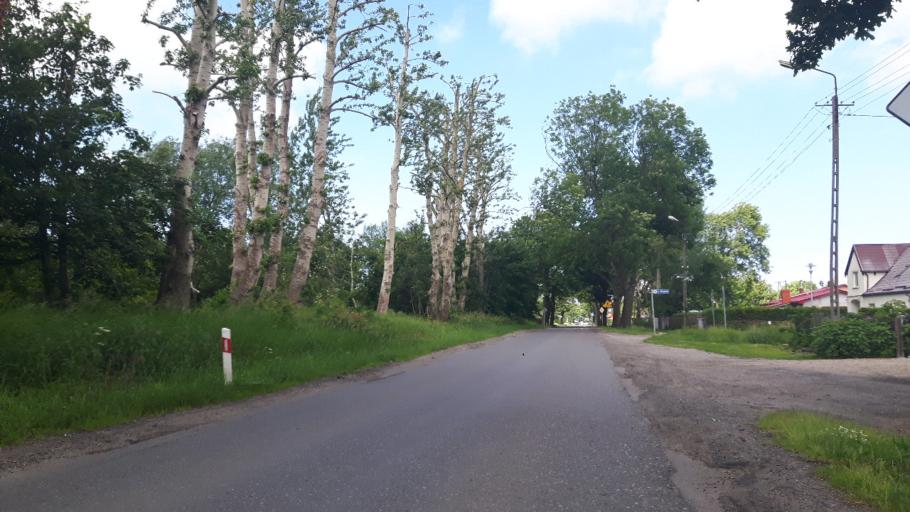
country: PL
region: Pomeranian Voivodeship
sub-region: Powiat slupski
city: Ustka
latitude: 54.5679
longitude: 16.8497
